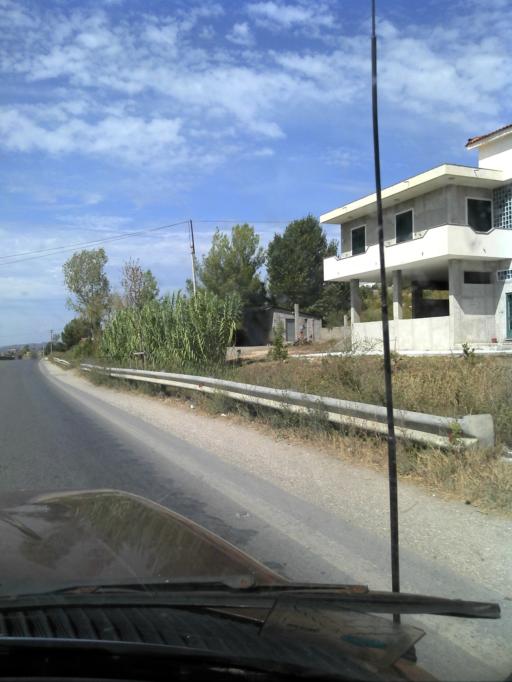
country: AL
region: Fier
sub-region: Rrethi i Lushnjes
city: Golem
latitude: 40.9974
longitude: 19.6667
